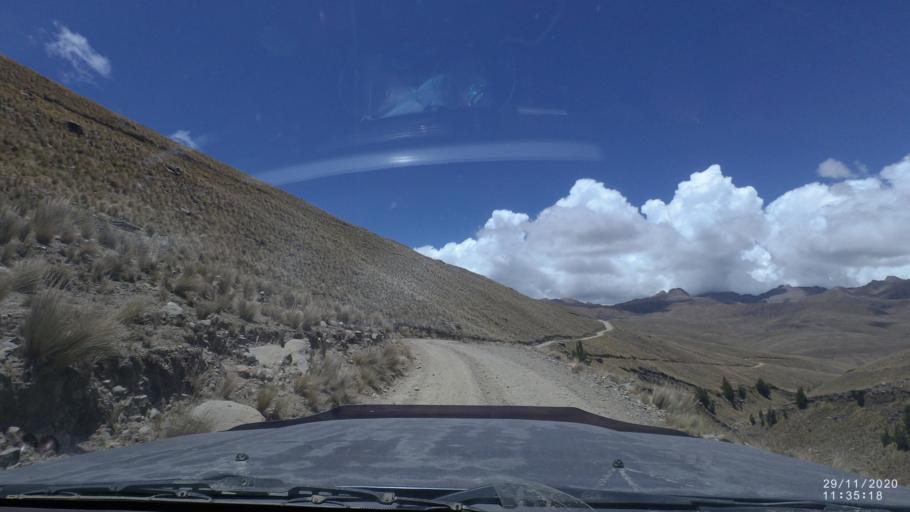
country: BO
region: Cochabamba
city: Cochabamba
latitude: -17.1926
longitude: -66.2234
